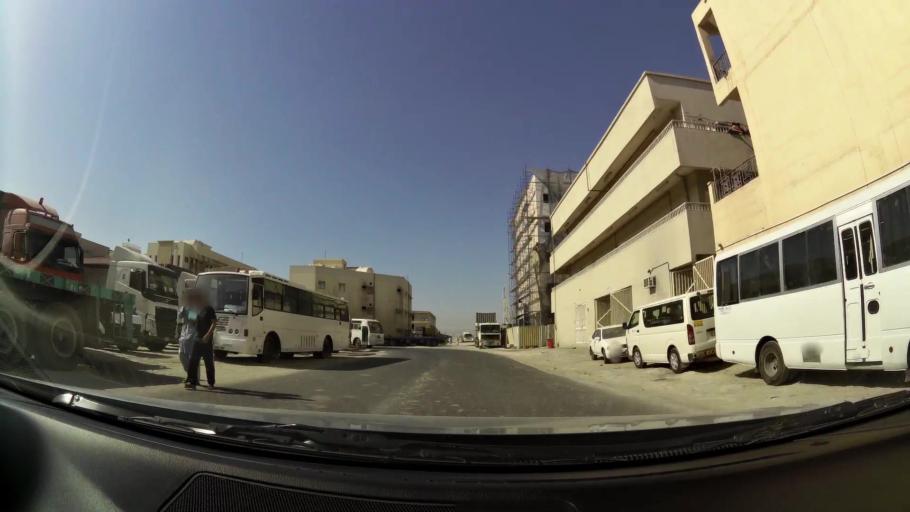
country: AE
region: Dubai
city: Dubai
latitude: 25.0083
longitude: 55.1113
